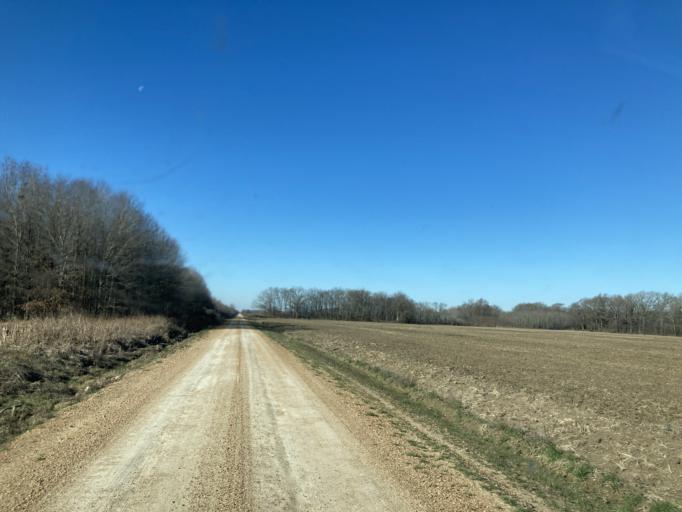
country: US
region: Mississippi
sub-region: Yazoo County
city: Yazoo City
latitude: 32.9519
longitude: -90.6106
